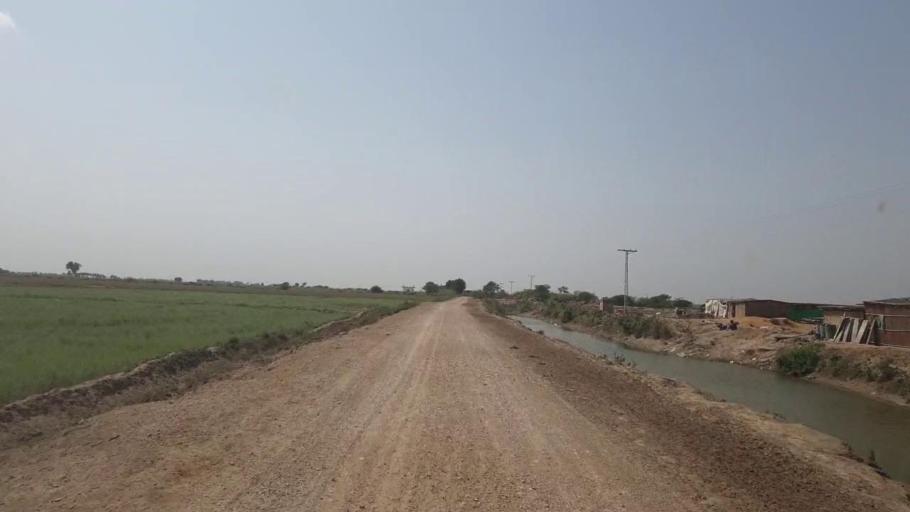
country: PK
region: Sindh
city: Jati
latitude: 24.4920
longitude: 68.5302
